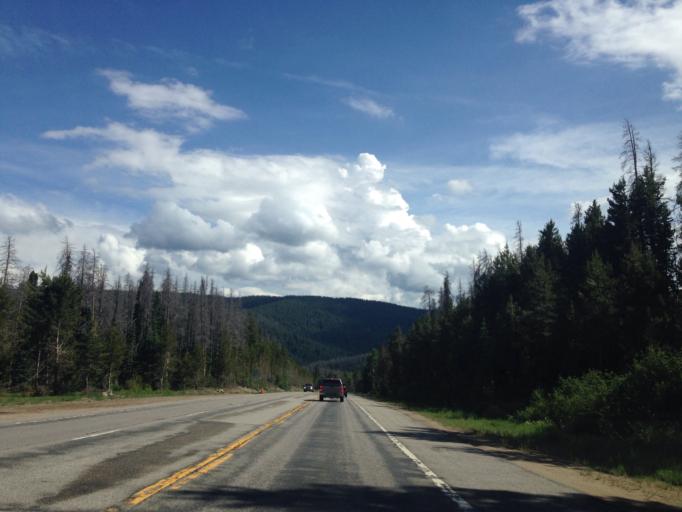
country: US
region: Colorado
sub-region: Routt County
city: Steamboat Springs
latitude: 40.3609
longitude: -106.7512
